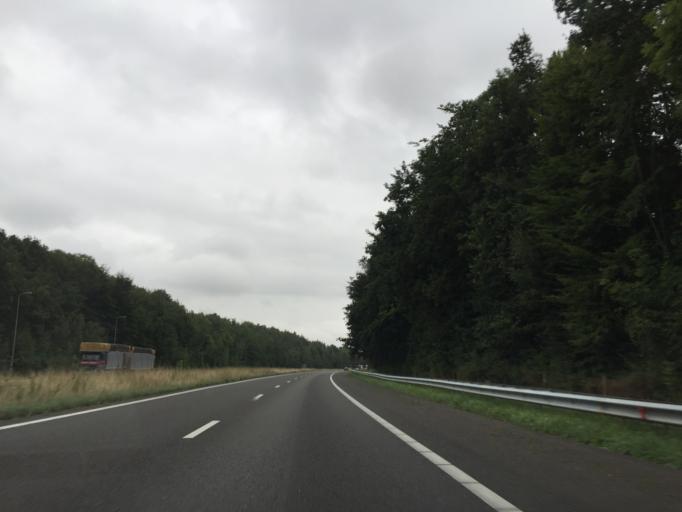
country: NL
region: Limburg
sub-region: Eijsden-Margraten
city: Eijsden
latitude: 50.7758
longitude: 5.7279
